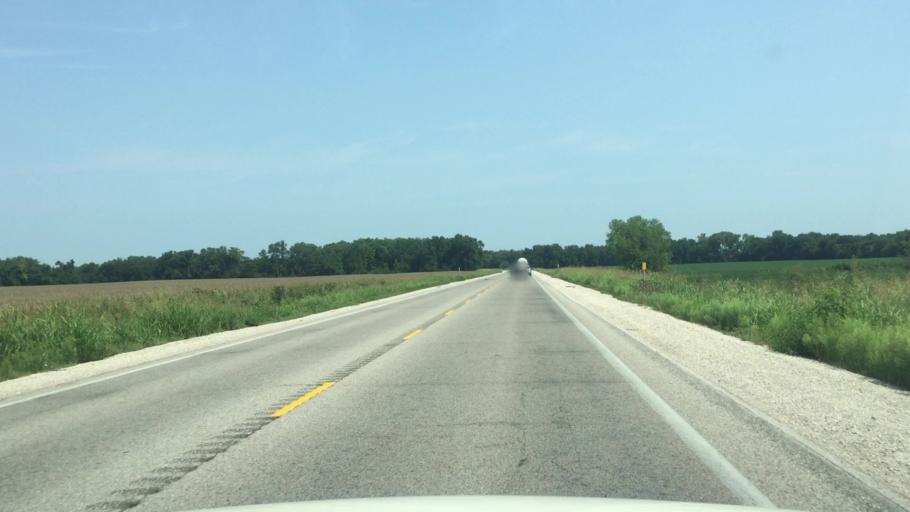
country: US
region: Kansas
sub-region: Montgomery County
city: Cherryvale
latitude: 37.1713
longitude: -95.5765
